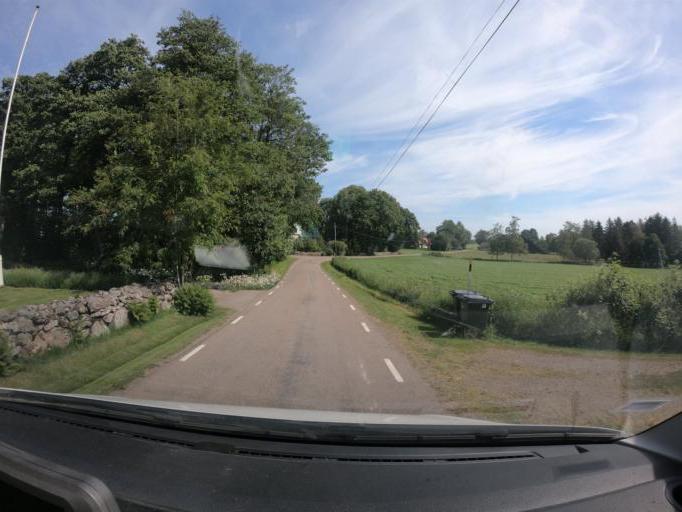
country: SE
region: Skane
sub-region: Bastads Kommun
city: Bastad
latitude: 56.4112
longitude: 12.8865
